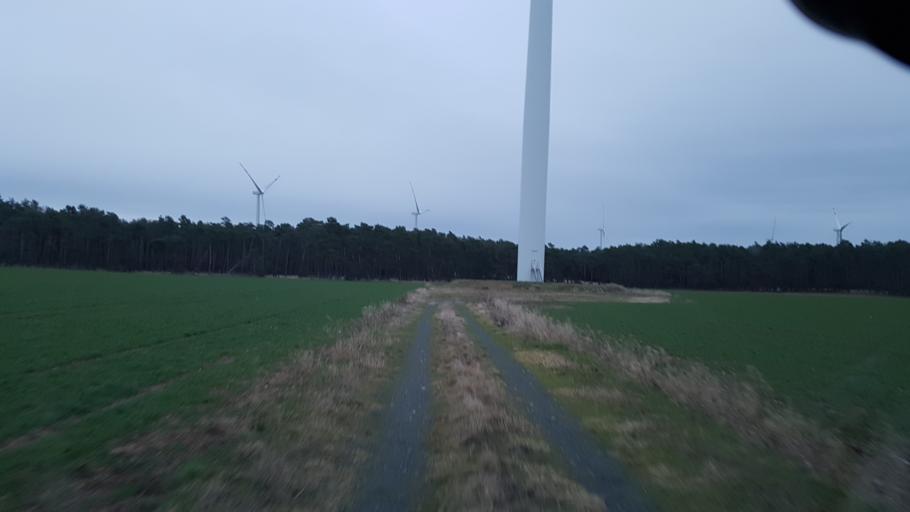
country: DE
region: Brandenburg
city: Schlieben
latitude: 51.6737
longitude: 13.3758
